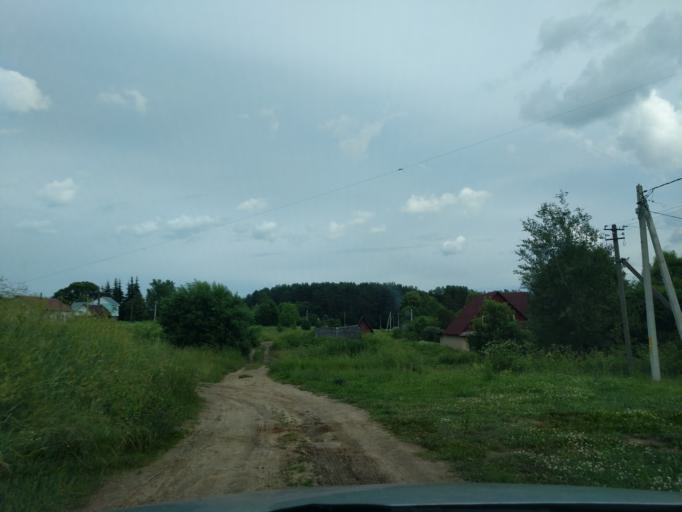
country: RU
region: Kaluga
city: Nikola-Lenivets
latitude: 54.7417
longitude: 35.6397
